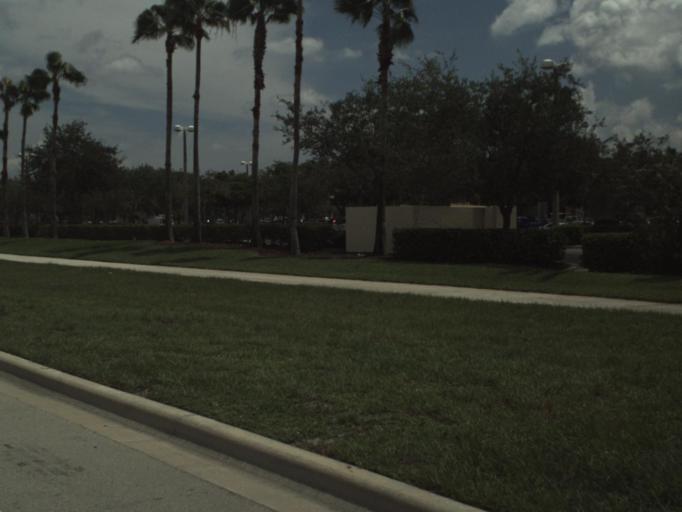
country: US
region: Florida
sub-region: Palm Beach County
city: Jupiter
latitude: 26.9320
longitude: -80.0934
